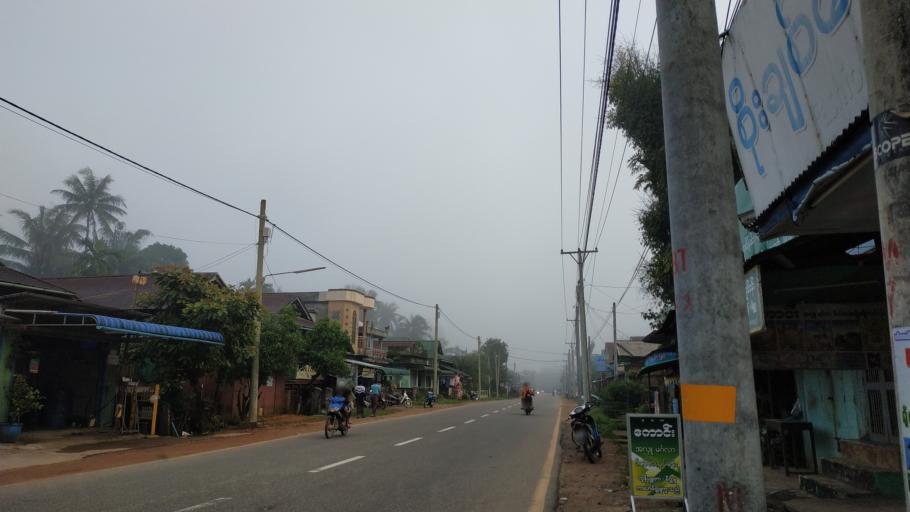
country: MM
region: Tanintharyi
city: Dawei
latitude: 14.0947
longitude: 98.1958
